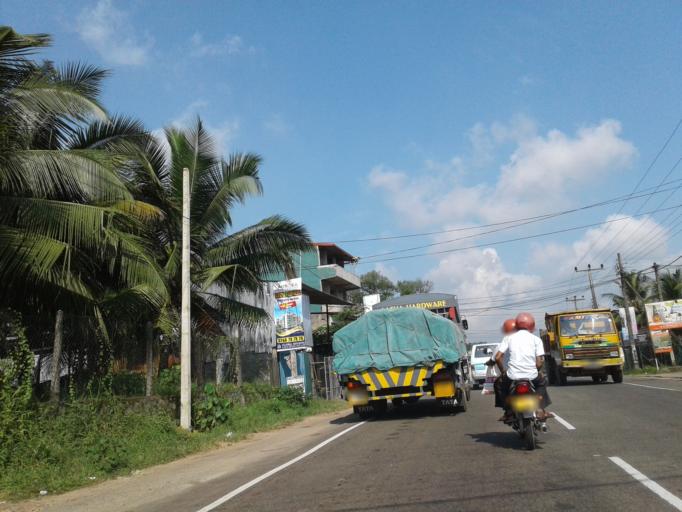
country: LK
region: Western
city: Battaramulla South
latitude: 6.8948
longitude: 79.9610
